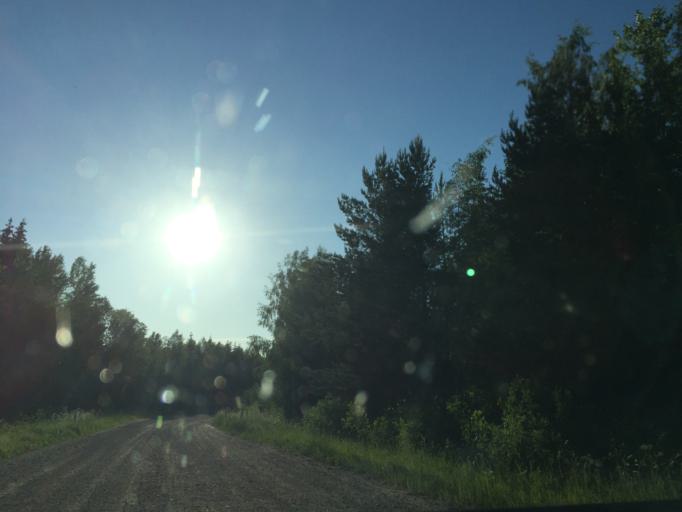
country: LV
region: Talsu Rajons
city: Sabile
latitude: 56.8656
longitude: 22.6444
